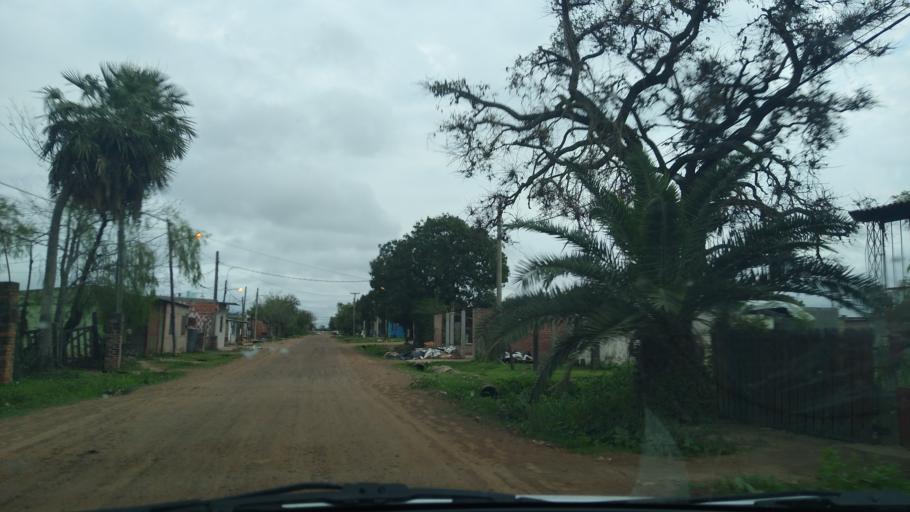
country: AR
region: Chaco
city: Barranqueras
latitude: -27.4745
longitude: -58.9209
